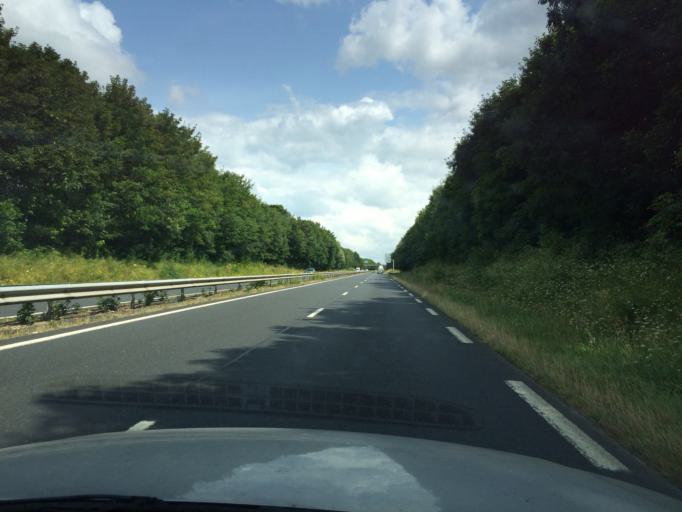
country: FR
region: Lower Normandy
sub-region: Departement du Calvados
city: Le Molay-Littry
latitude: 49.3321
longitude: -0.9087
